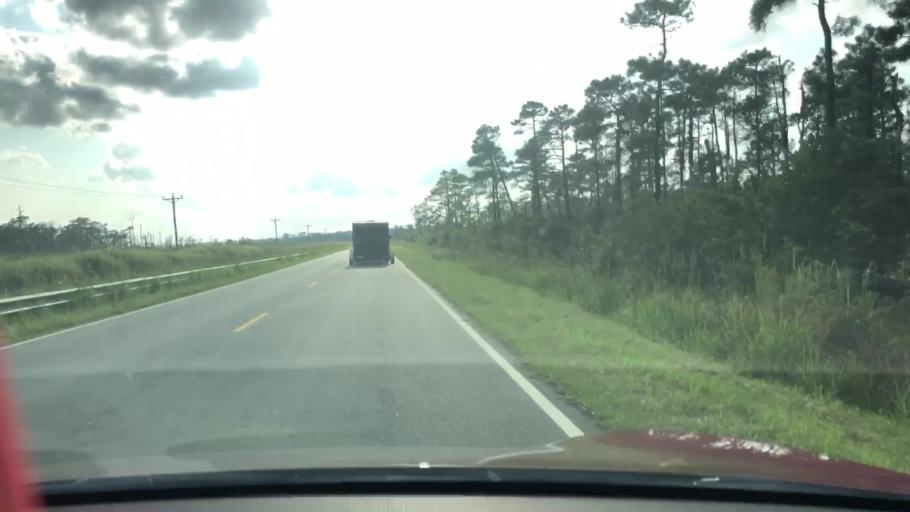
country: US
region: North Carolina
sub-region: Dare County
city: Wanchese
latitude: 35.6083
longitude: -75.8047
